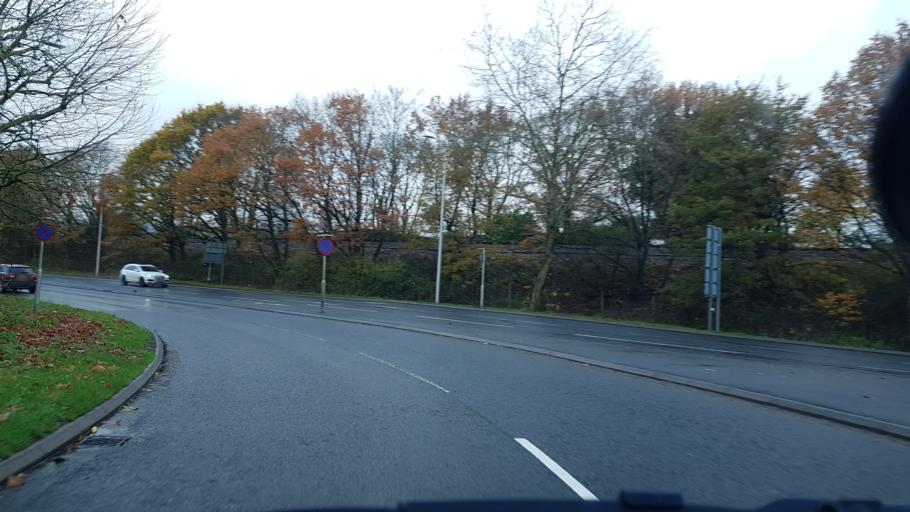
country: GB
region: England
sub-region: Bracknell Forest
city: Bracknell
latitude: 51.4131
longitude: -0.7617
